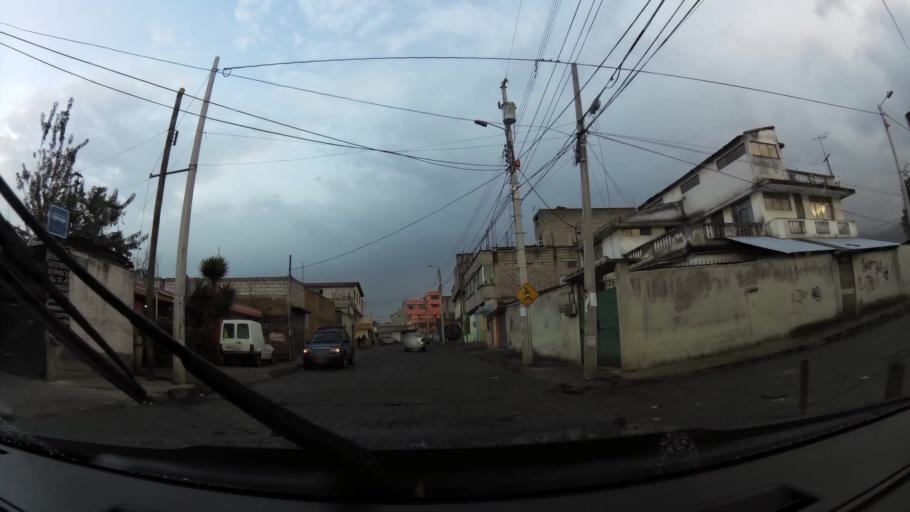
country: EC
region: Pichincha
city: Quito
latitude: -0.2961
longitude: -78.5380
